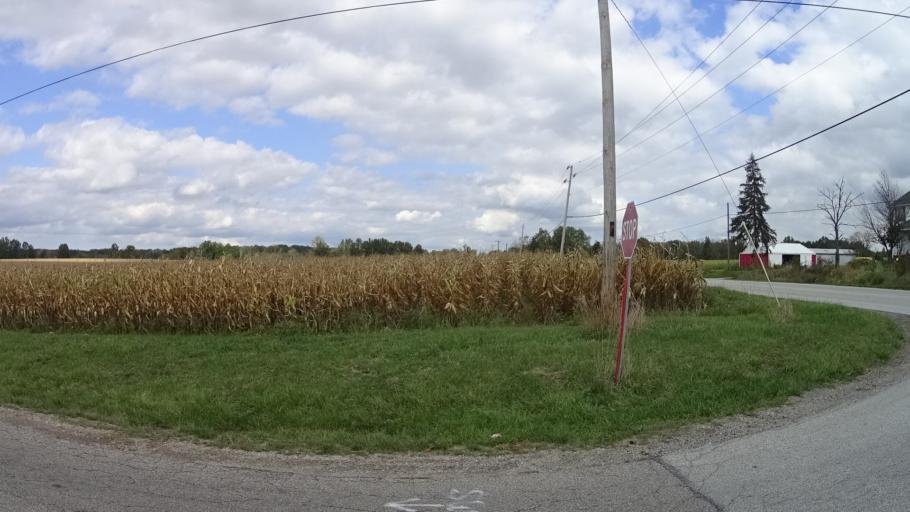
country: US
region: Ohio
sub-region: Lorain County
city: Eaton Estates
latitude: 41.2943
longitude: -82.0017
